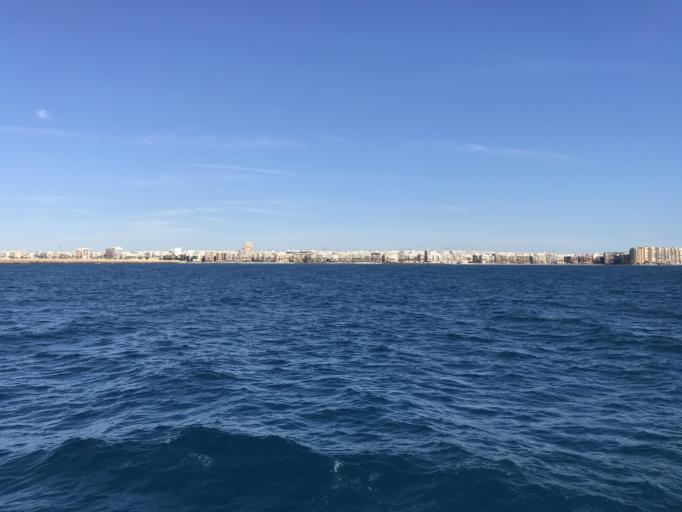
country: ES
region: Valencia
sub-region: Provincia de Alicante
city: Torrevieja
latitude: 37.9639
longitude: -0.6712
